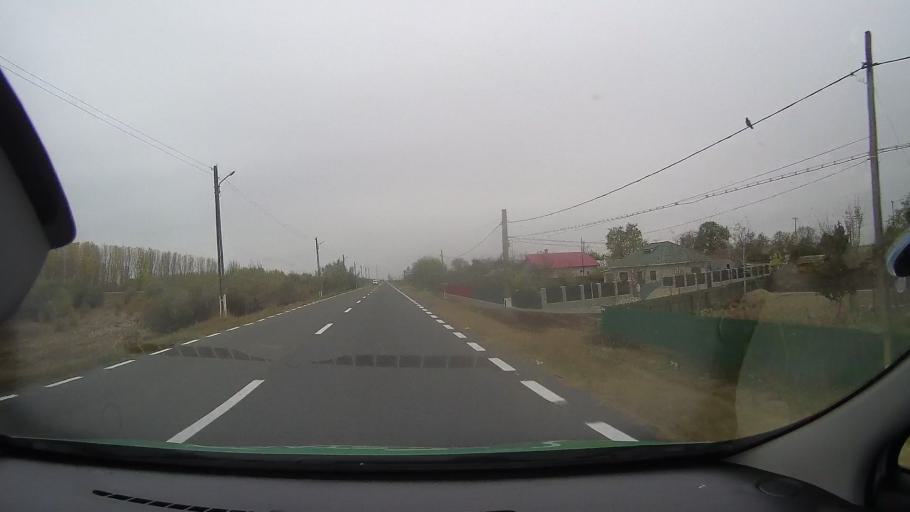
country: RO
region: Ialomita
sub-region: Comuna Giurgeni
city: Giurgeni
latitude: 44.7355
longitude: 27.8551
